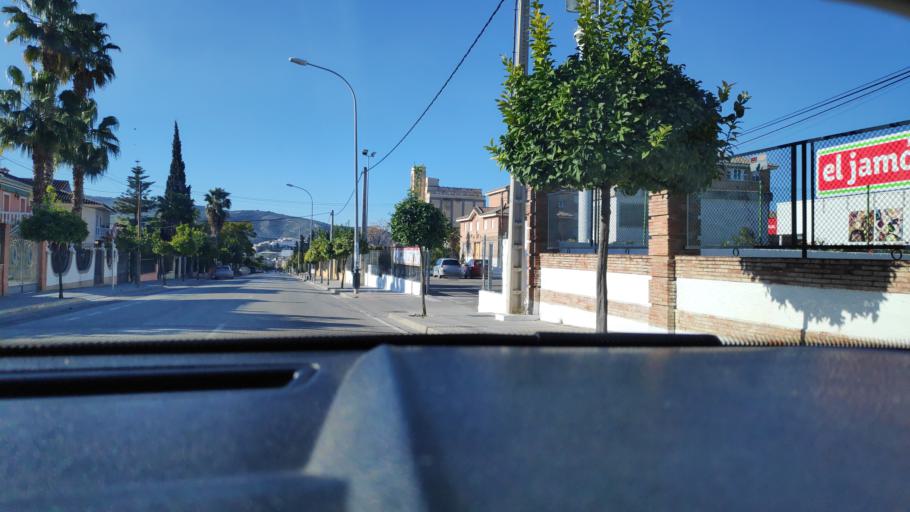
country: ES
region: Andalusia
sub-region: Province of Cordoba
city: Baena
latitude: 37.6215
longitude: -4.3125
